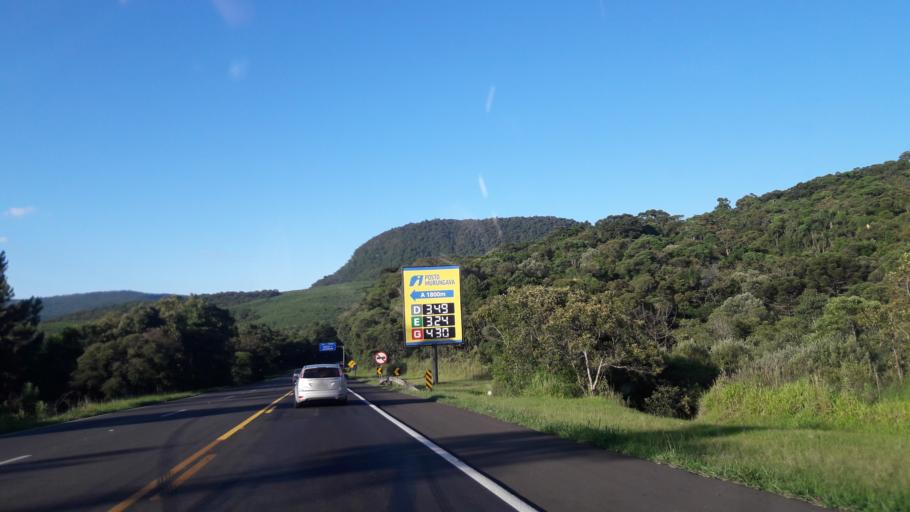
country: BR
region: Parana
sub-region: Prudentopolis
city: Prudentopolis
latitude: -25.3169
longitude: -51.1888
